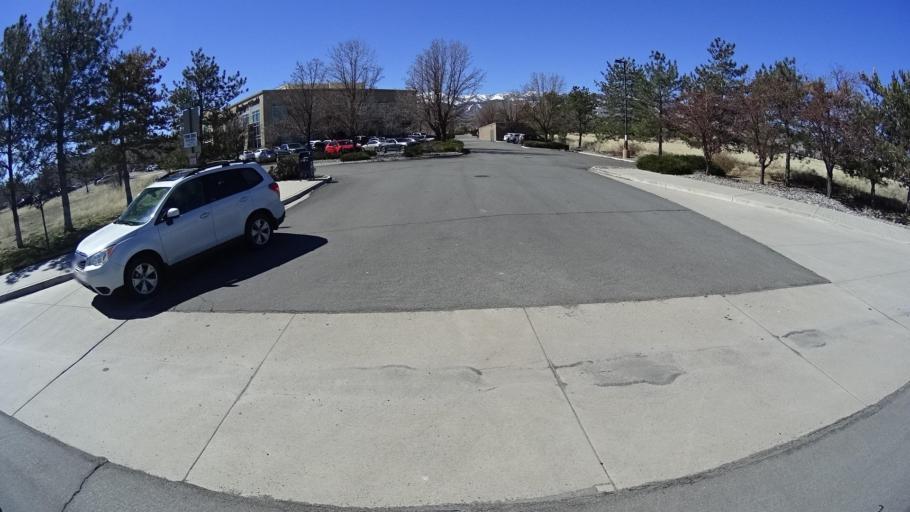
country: US
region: Nevada
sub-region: Washoe County
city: Sparks
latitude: 39.4335
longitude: -119.7571
